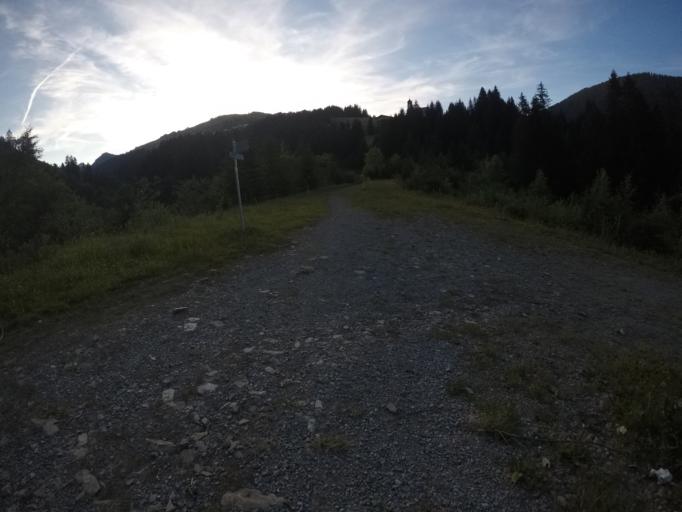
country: AT
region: Vorarlberg
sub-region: Politischer Bezirk Bregenz
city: Damuels
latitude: 47.2777
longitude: 9.8928
